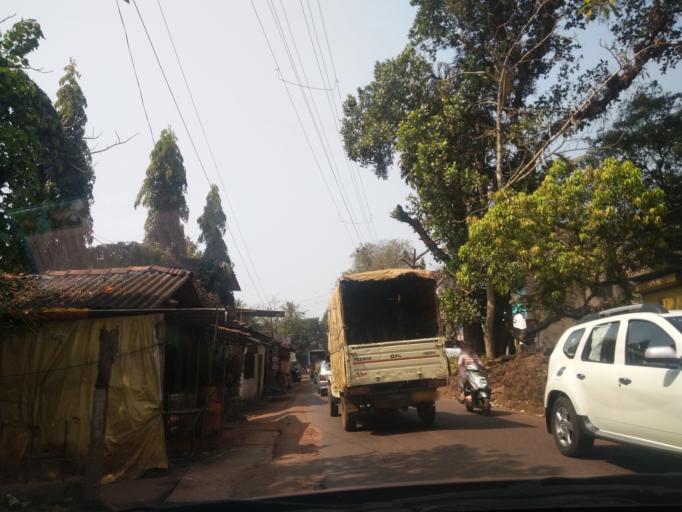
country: IN
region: Goa
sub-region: North Goa
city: Aldona
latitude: 15.6193
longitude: 73.9030
